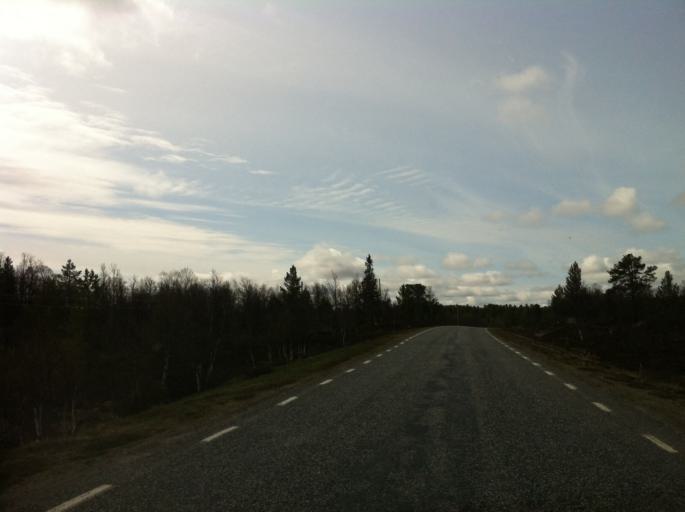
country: NO
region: Hedmark
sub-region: Engerdal
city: Engerdal
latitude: 62.3648
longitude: 12.7904
